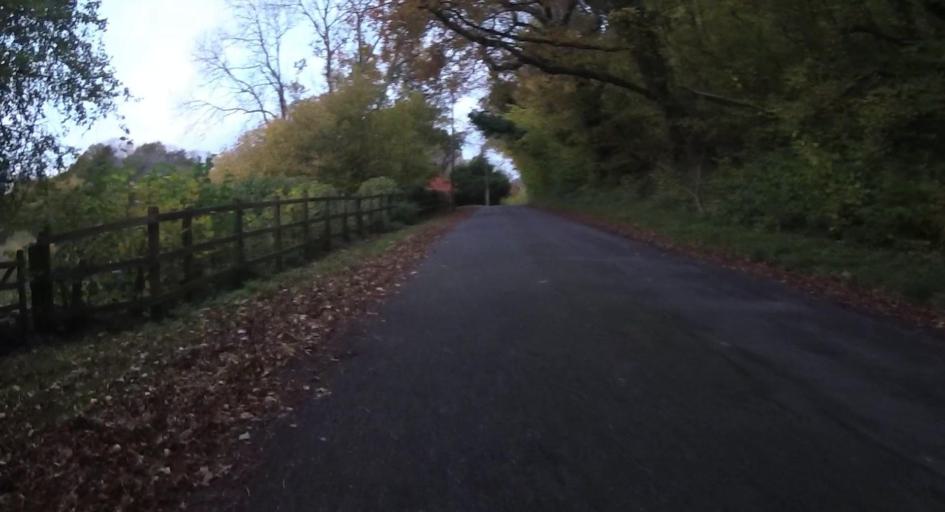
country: GB
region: England
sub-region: Hampshire
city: Kingsley
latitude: 51.1485
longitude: -0.8800
